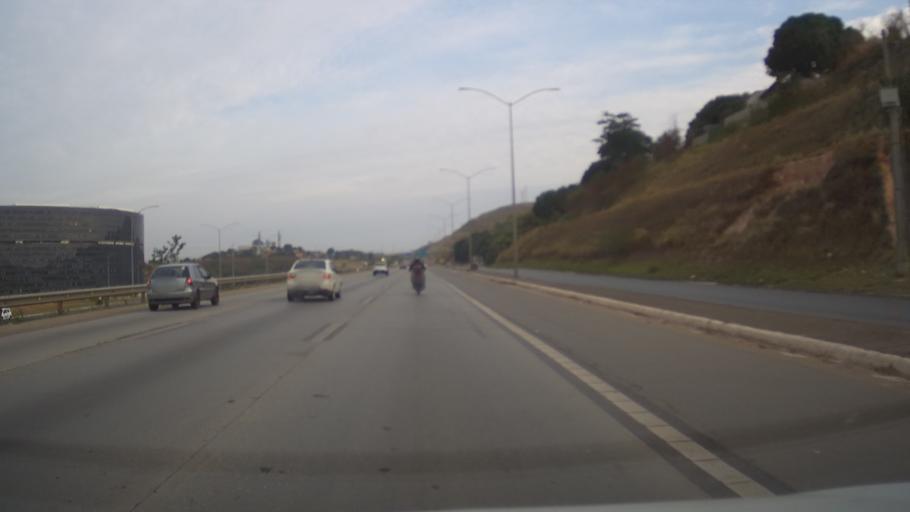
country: BR
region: Minas Gerais
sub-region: Vespasiano
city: Vespasiano
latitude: -19.7876
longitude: -43.9488
